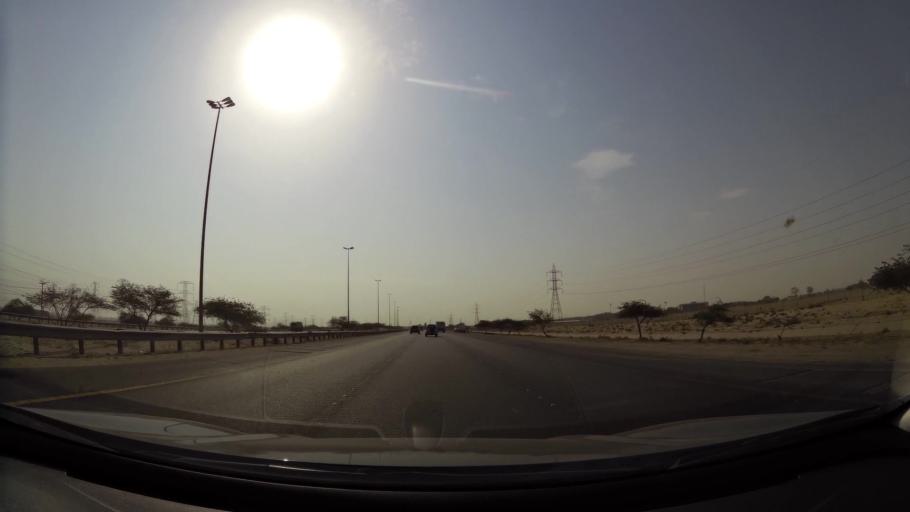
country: KW
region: Al Ahmadi
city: Al Ahmadi
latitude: 28.9694
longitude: 48.1144
